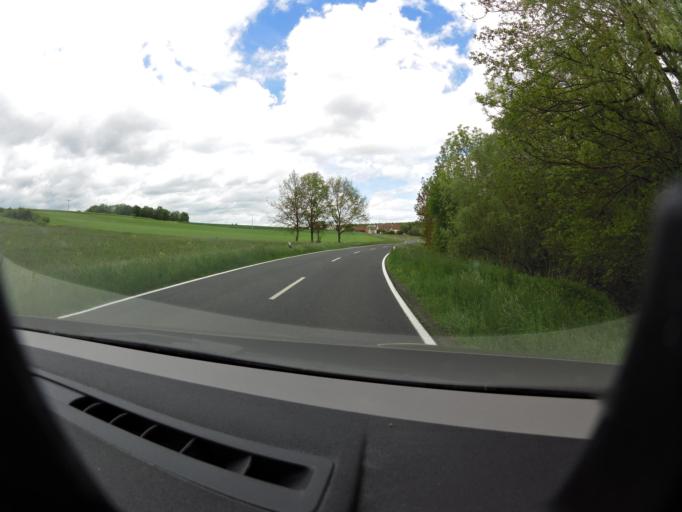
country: DE
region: Bavaria
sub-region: Regierungsbezirk Unterfranken
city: Prosselsheim
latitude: 49.8349
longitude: 10.1467
